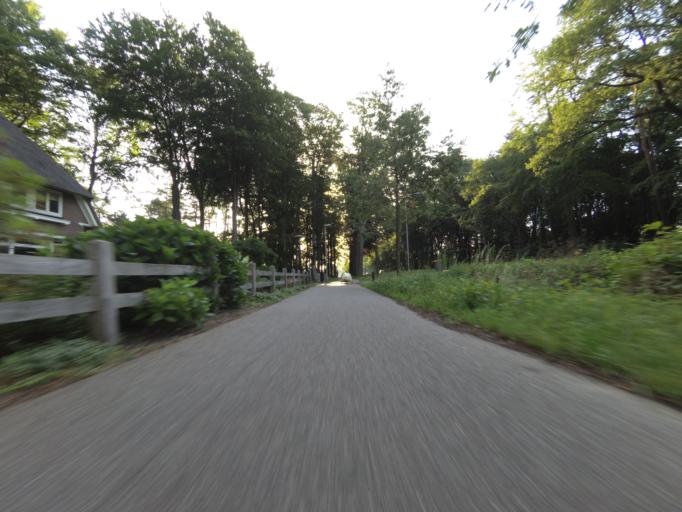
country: NL
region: Gelderland
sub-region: Gemeente Lochem
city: Epse
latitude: 52.2492
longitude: 6.2248
